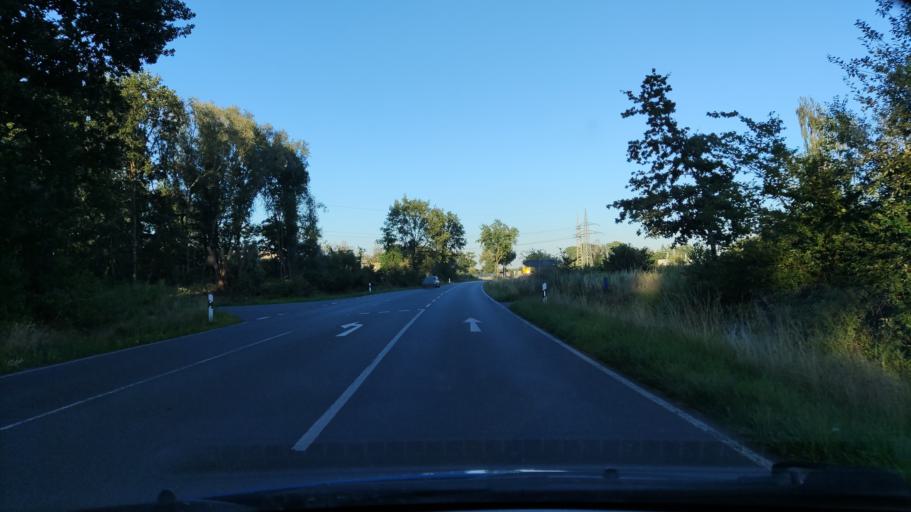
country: DE
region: Lower Saxony
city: Luechow
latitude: 52.9819
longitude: 11.1583
